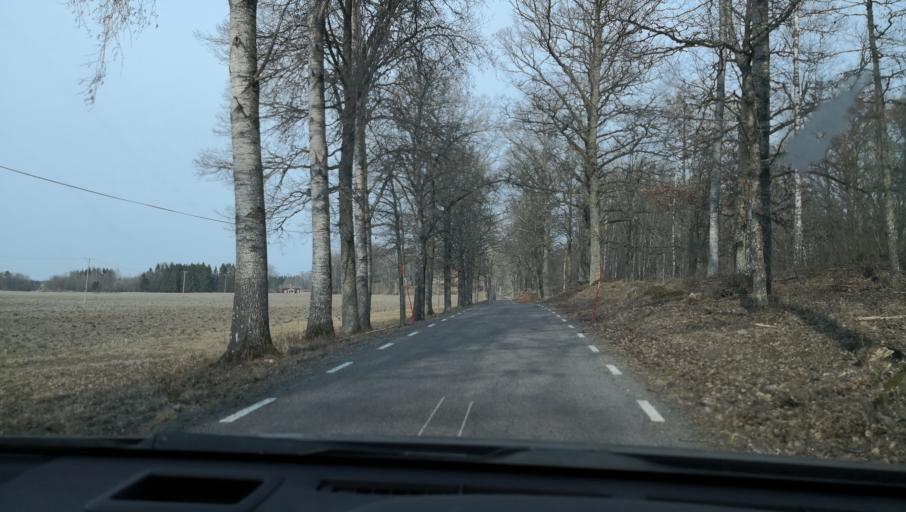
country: SE
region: OErebro
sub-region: Lindesbergs Kommun
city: Frovi
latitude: 59.4009
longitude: 15.4139
